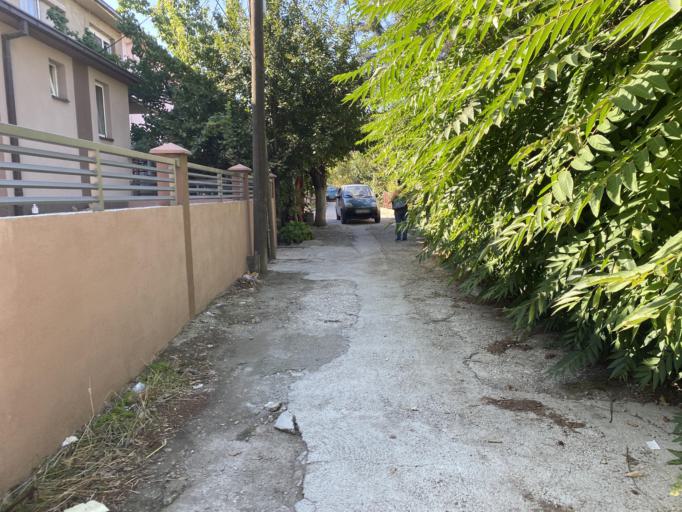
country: MK
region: Veles
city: Veles
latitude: 41.7178
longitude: 21.7685
